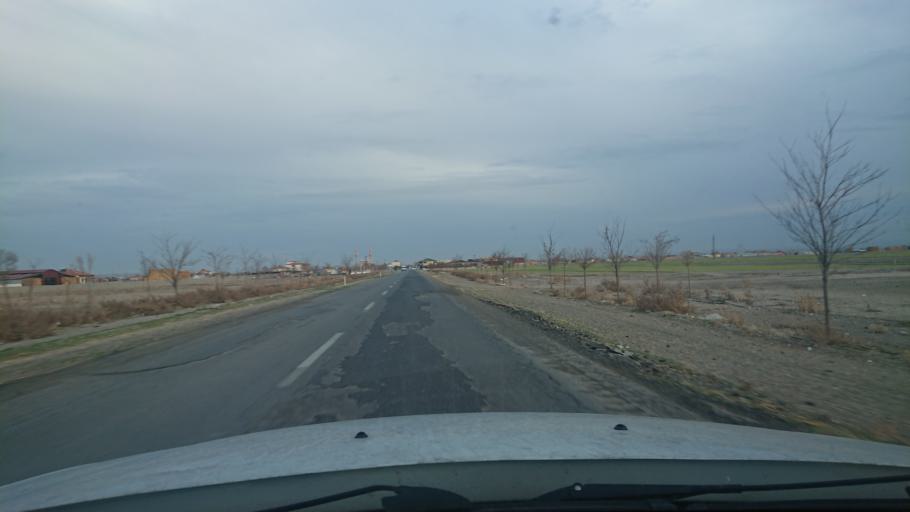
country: TR
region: Aksaray
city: Yesilova
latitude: 38.3279
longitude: 33.7527
